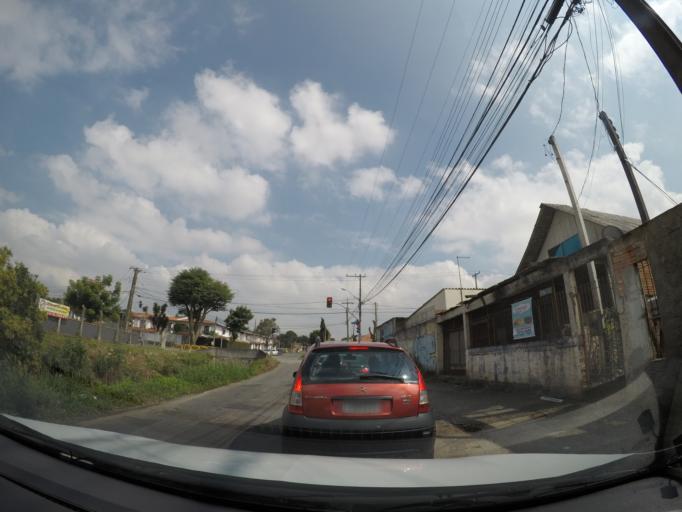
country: BR
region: Parana
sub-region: Sao Jose Dos Pinhais
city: Sao Jose dos Pinhais
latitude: -25.4906
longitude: -49.2550
